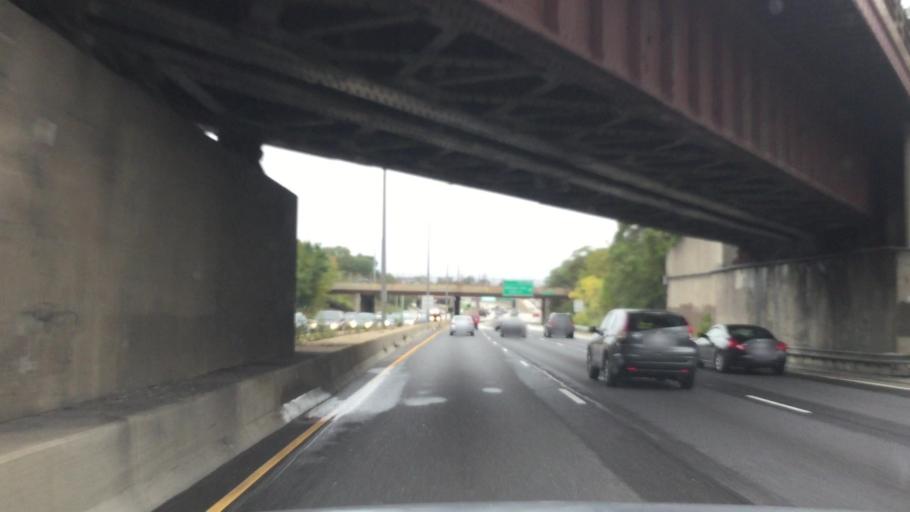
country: US
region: Illinois
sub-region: Cook County
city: Lincolnwood
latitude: 41.9696
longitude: -87.7473
